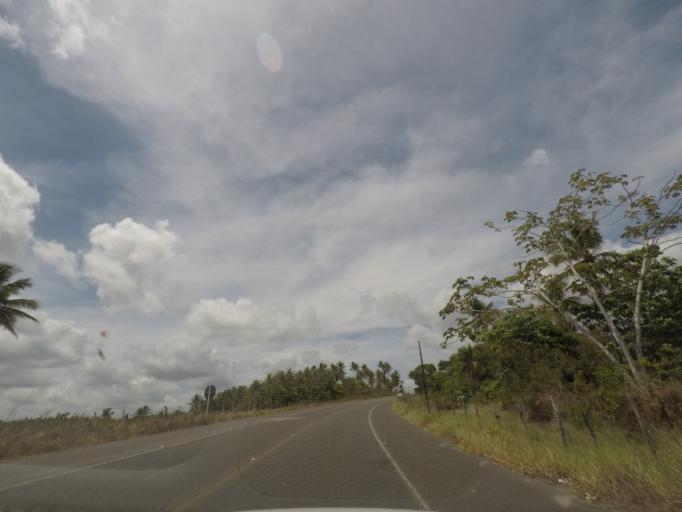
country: BR
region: Sergipe
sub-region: Indiaroba
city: Indiaroba
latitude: -11.5254
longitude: -37.5291
